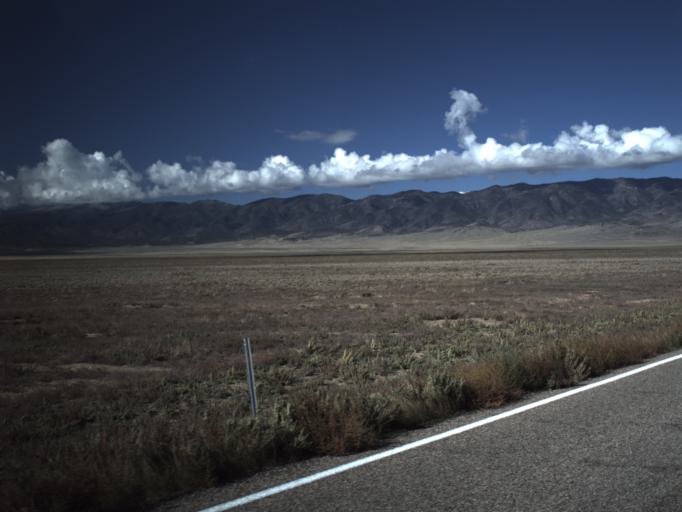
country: US
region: Utah
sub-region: Beaver County
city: Milford
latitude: 38.4598
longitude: -113.3741
